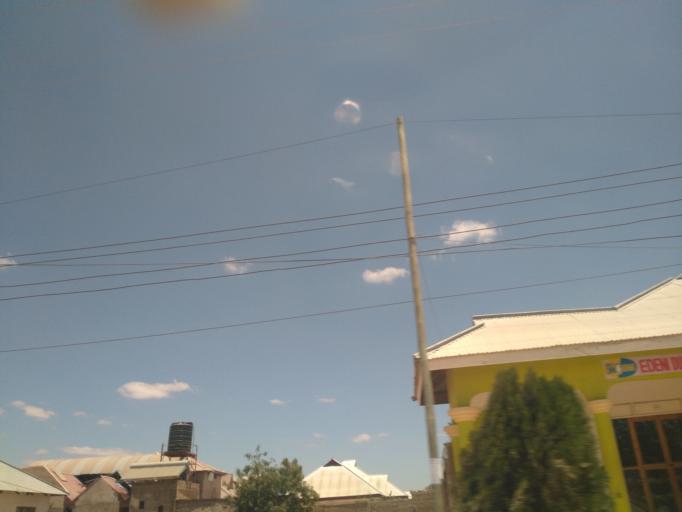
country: TZ
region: Dodoma
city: Dodoma
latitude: -6.1460
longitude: 35.7383
